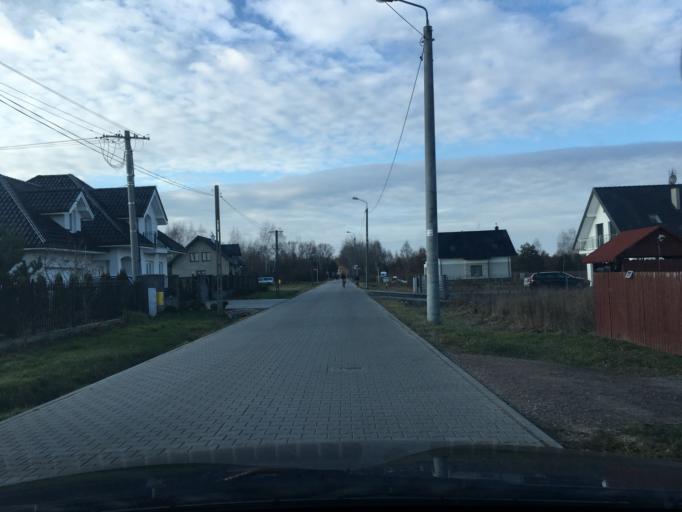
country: PL
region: Masovian Voivodeship
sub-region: Powiat piaseczynski
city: Lesznowola
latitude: 52.0259
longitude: 20.9437
